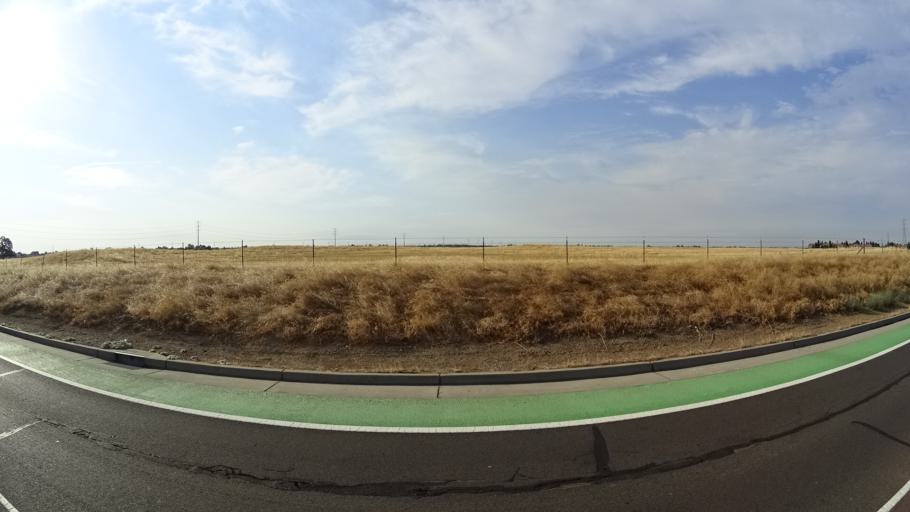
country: US
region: California
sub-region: Sacramento County
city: Laguna
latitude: 38.4083
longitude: -121.4587
